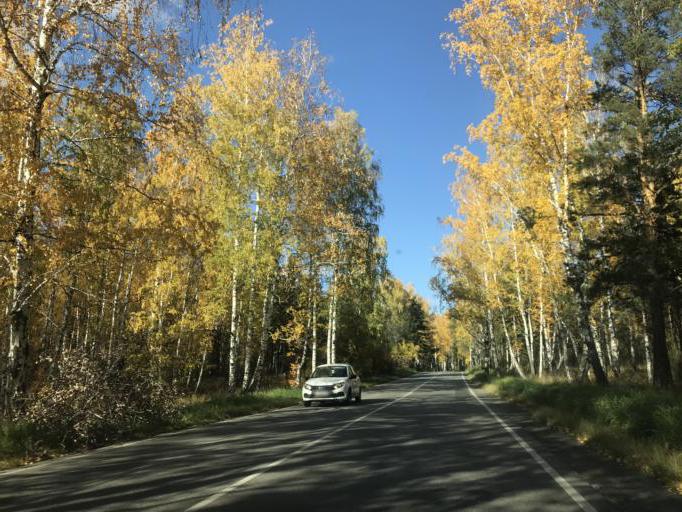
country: RU
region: Chelyabinsk
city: Dolgoderevenskoye
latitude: 55.2760
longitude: 61.3649
